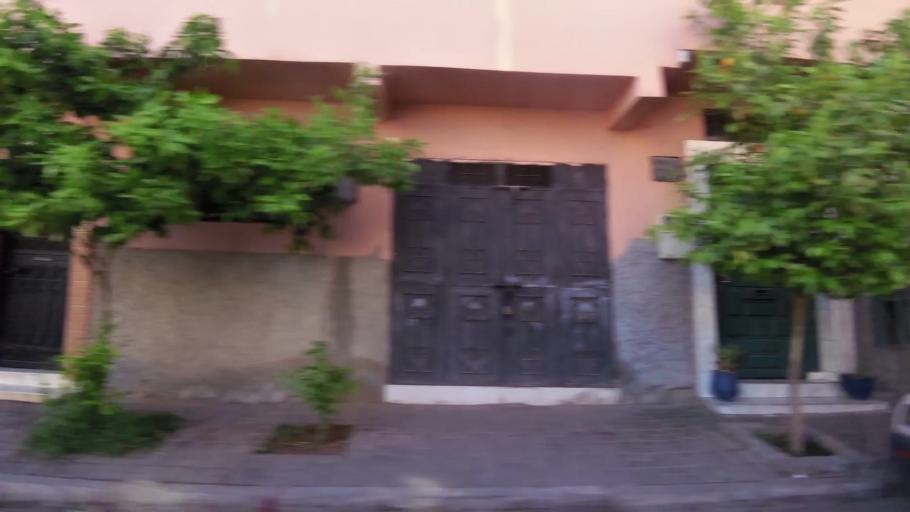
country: MA
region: Marrakech-Tensift-Al Haouz
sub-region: Marrakech
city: Marrakesh
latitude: 31.5986
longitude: -8.0304
